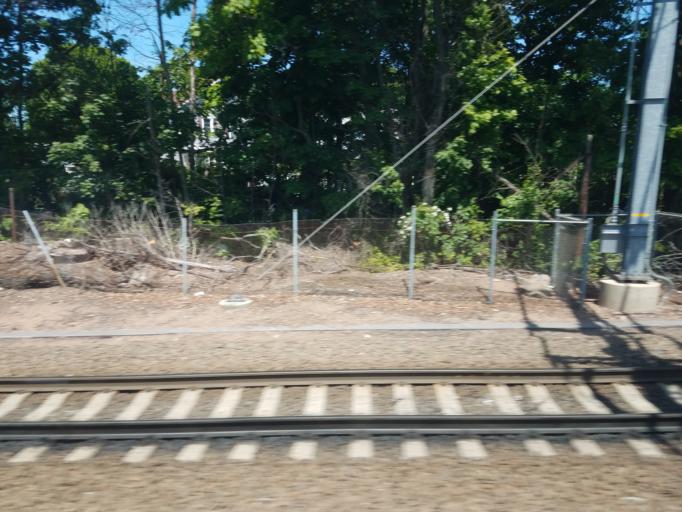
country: US
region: Connecticut
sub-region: New Haven County
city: New Haven
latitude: 41.3122
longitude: -72.9080
